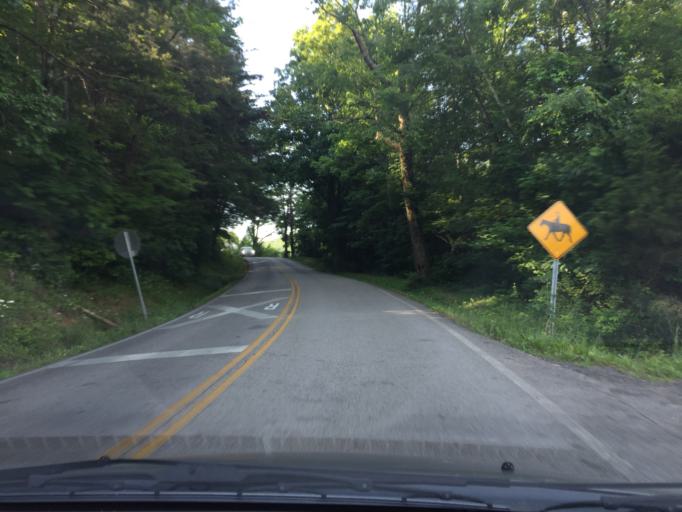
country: US
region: Tennessee
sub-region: Hamilton County
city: Collegedale
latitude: 35.0873
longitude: -85.0120
